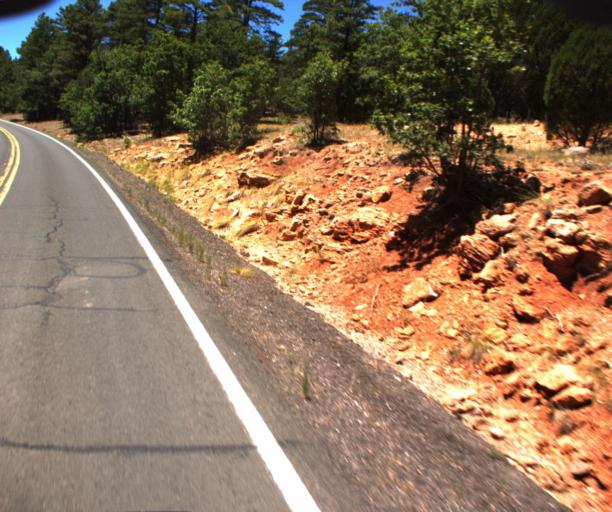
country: US
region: Arizona
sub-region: Gila County
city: Pine
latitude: 34.5942
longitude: -111.2477
